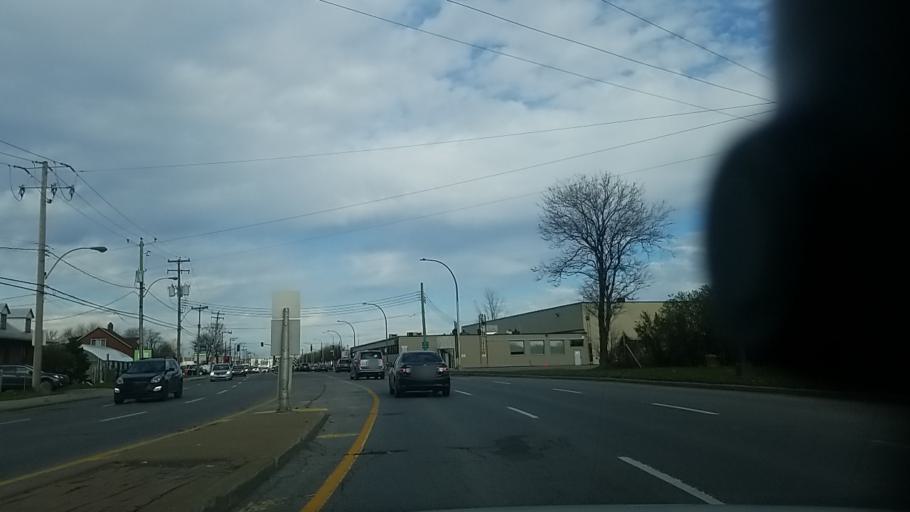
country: CA
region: Quebec
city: Saint-Laurent
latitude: 45.5123
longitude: -73.7218
